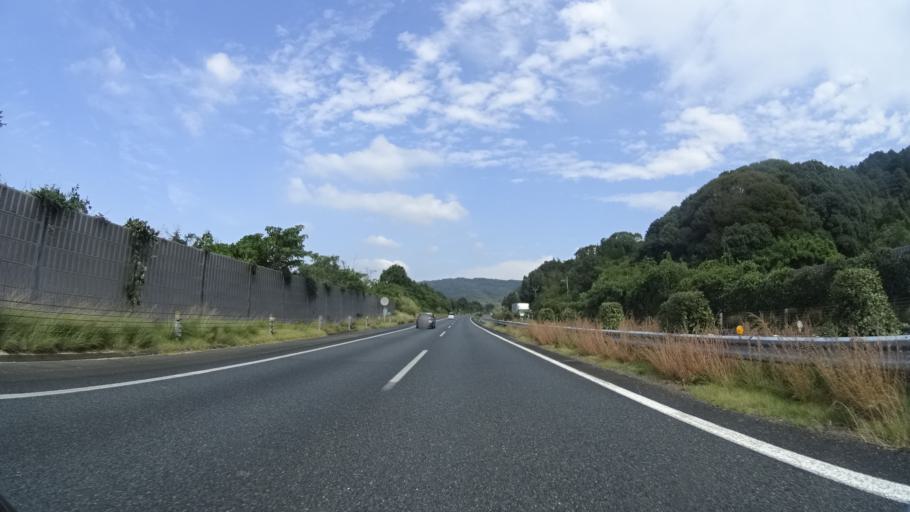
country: JP
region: Kumamoto
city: Matsubase
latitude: 32.6018
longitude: 130.7206
